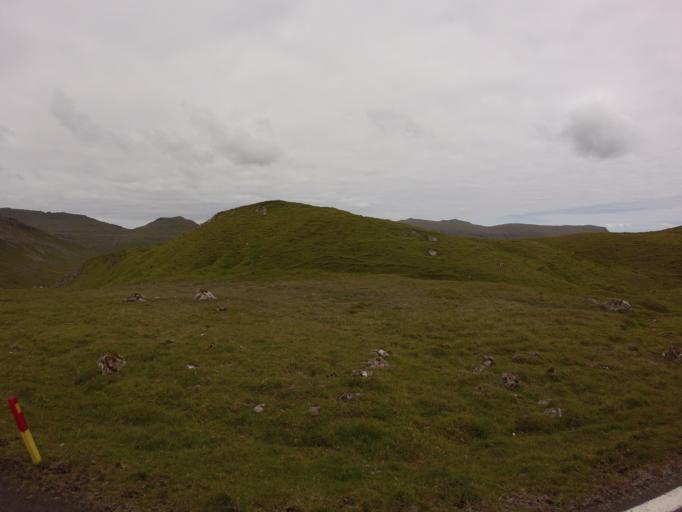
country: FO
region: Suduroy
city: Tvoroyri
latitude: 61.5240
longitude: -6.8295
